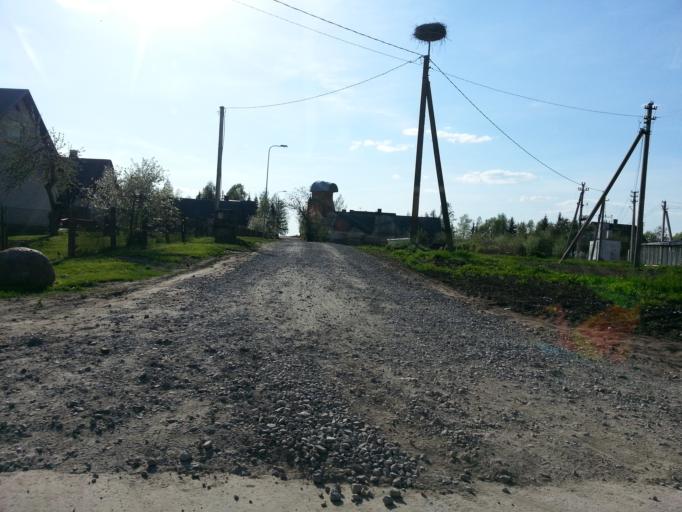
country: LT
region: Panevezys
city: Pasvalys
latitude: 55.9346
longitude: 24.3401
